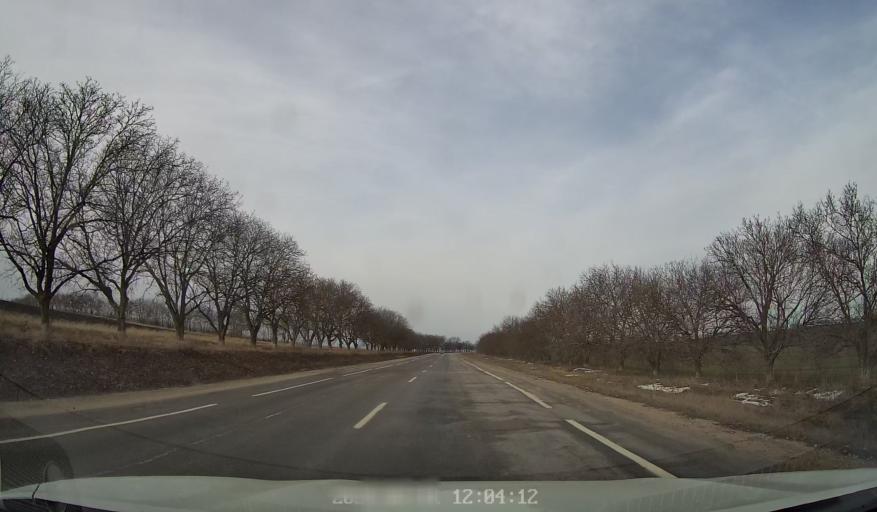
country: MD
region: Riscani
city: Riscani
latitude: 47.9665
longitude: 27.5982
